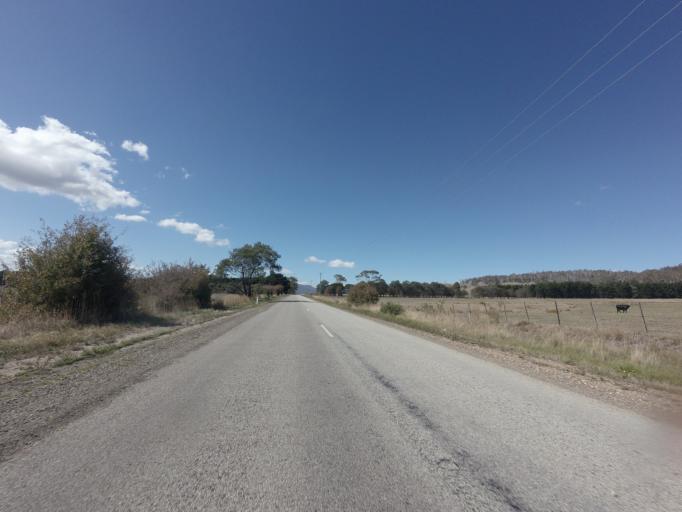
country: AU
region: Tasmania
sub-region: Break O'Day
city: St Helens
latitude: -41.6189
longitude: 148.0048
